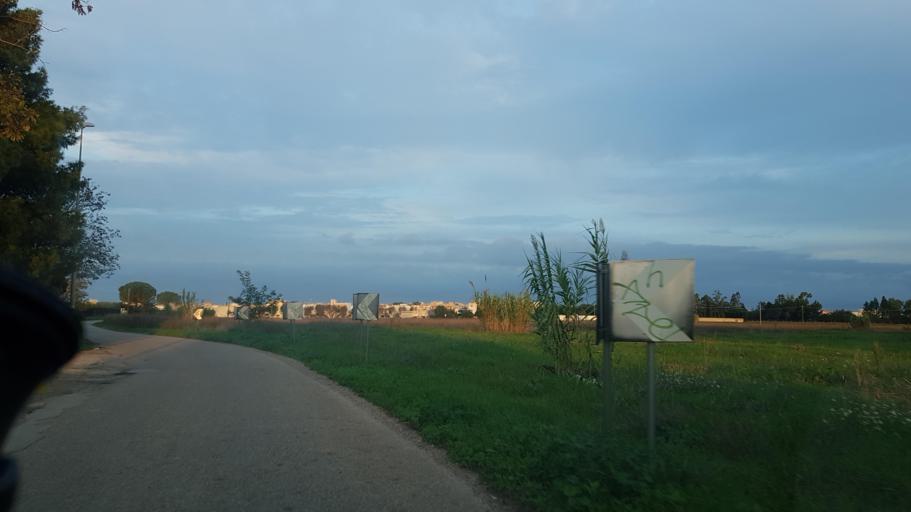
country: IT
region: Apulia
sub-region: Provincia di Brindisi
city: Mesagne
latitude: 40.5515
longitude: 17.7972
